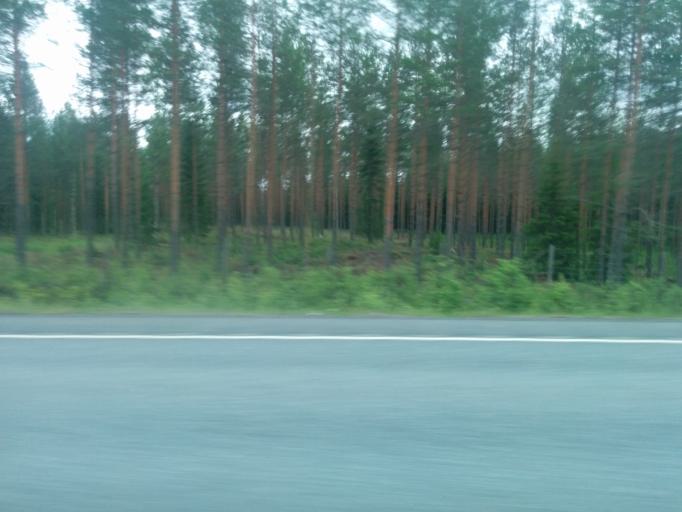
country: FI
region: Pirkanmaa
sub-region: Tampere
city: Orivesi
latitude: 61.6663
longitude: 24.2723
